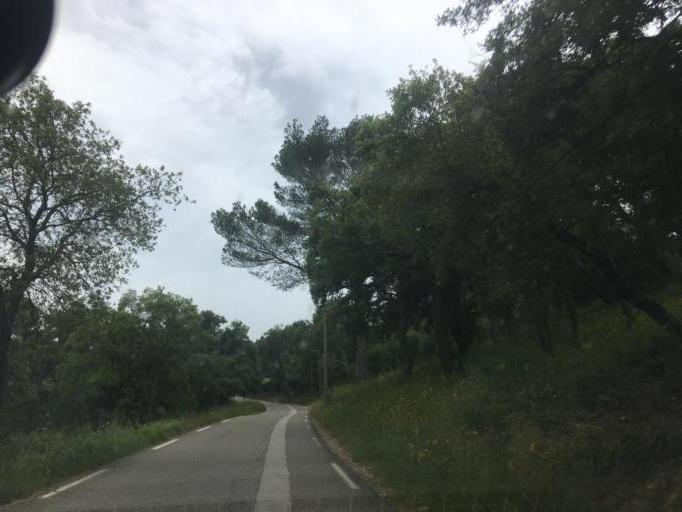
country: FR
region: Provence-Alpes-Cote d'Azur
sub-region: Departement du Var
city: La Londe-les-Maures
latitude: 43.1690
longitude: 6.2160
